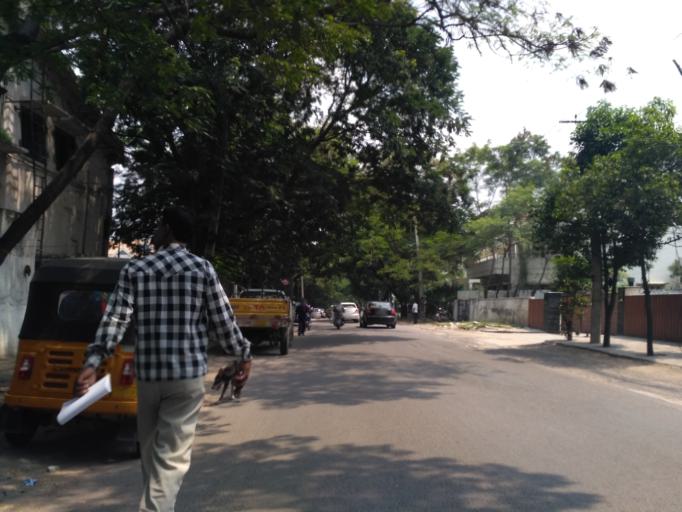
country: IN
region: Telangana
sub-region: Rangareddi
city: Kukatpalli
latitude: 17.4291
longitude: 78.4141
